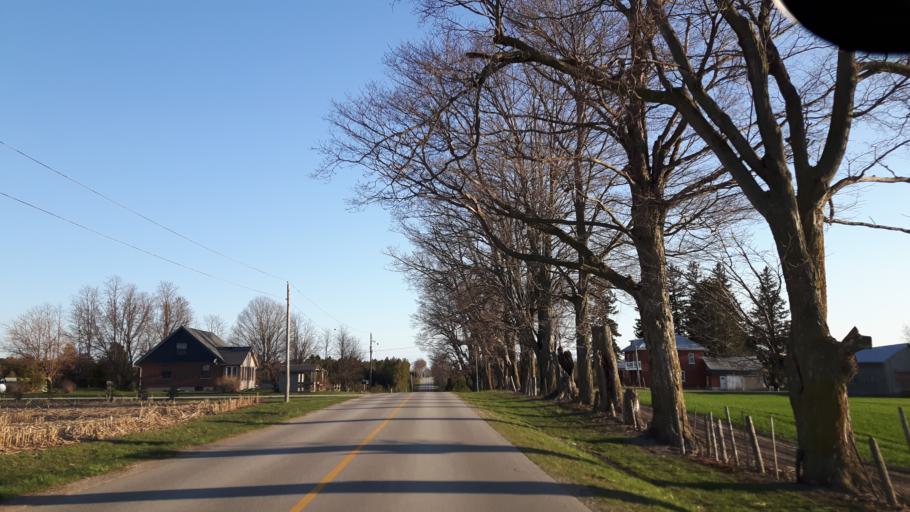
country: CA
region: Ontario
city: Goderich
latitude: 43.6704
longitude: -81.6847
